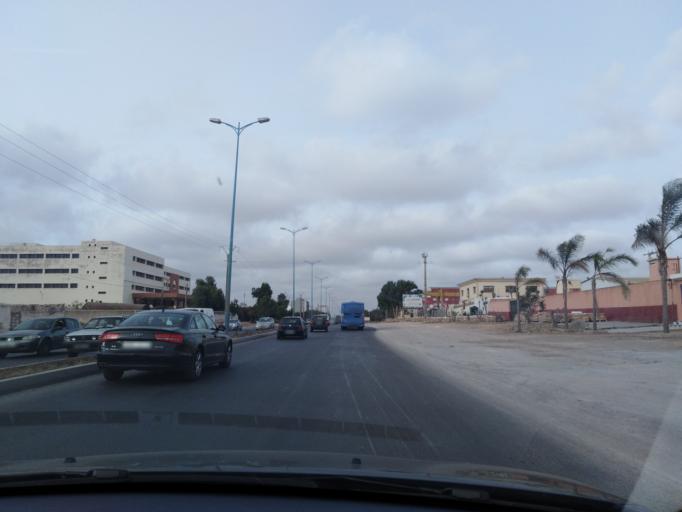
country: MA
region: Grand Casablanca
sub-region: Nouaceur
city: Bouskoura
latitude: 33.5218
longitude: -7.6890
